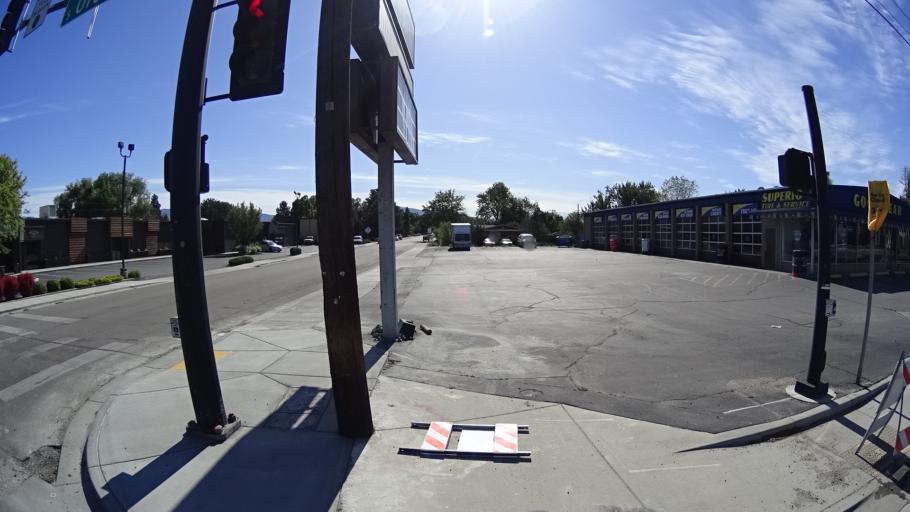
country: US
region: Idaho
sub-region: Ada County
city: Garden City
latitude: 43.5914
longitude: -116.2435
